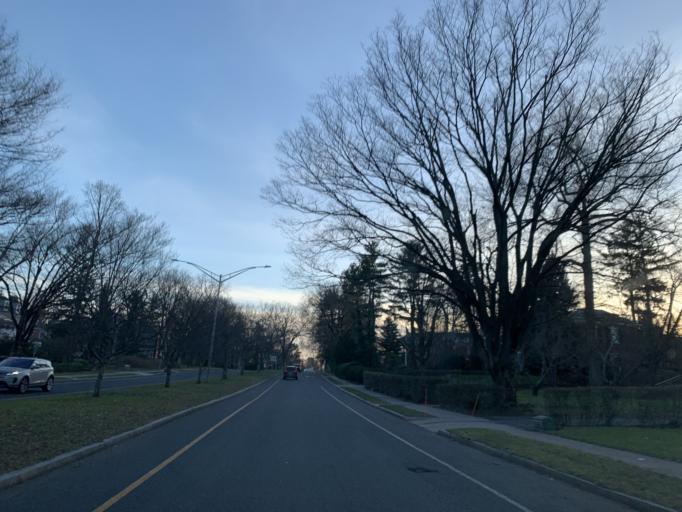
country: US
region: Connecticut
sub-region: Hartford County
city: Hartford
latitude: 41.7782
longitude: -72.7099
